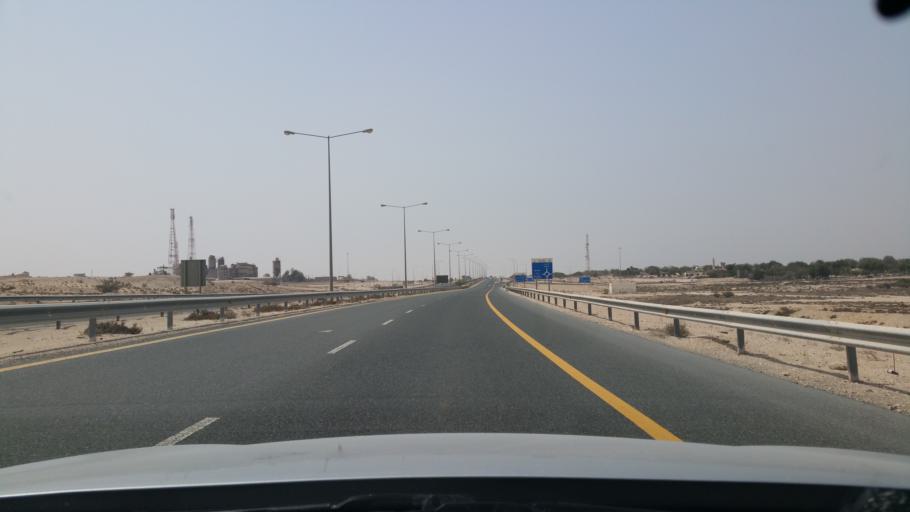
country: QA
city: Umm Bab
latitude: 25.2166
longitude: 50.8075
